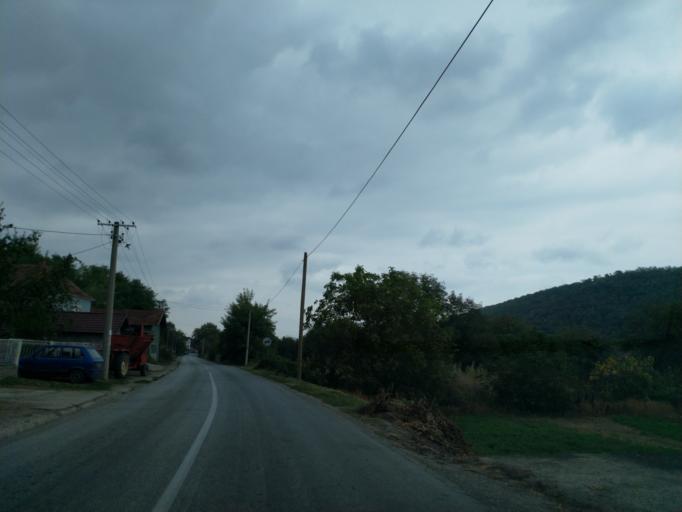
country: RS
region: Central Serbia
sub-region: Pomoravski Okrug
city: Jagodina
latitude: 44.0698
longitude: 21.1788
